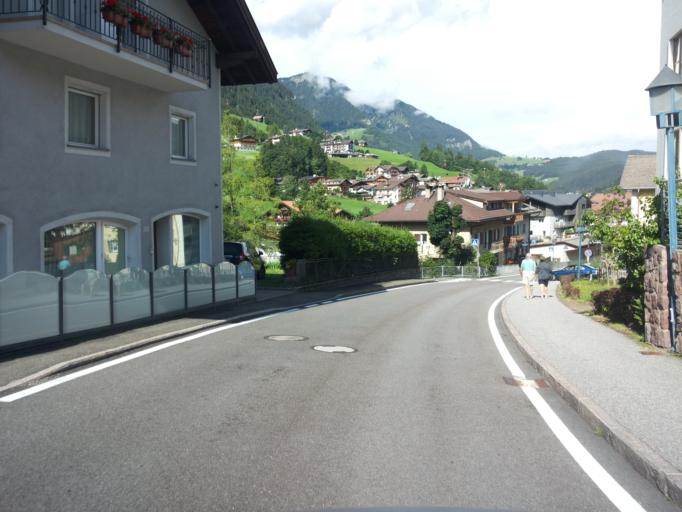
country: IT
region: Trentino-Alto Adige
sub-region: Bolzano
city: Ortisei
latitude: 46.5714
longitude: 11.6788
